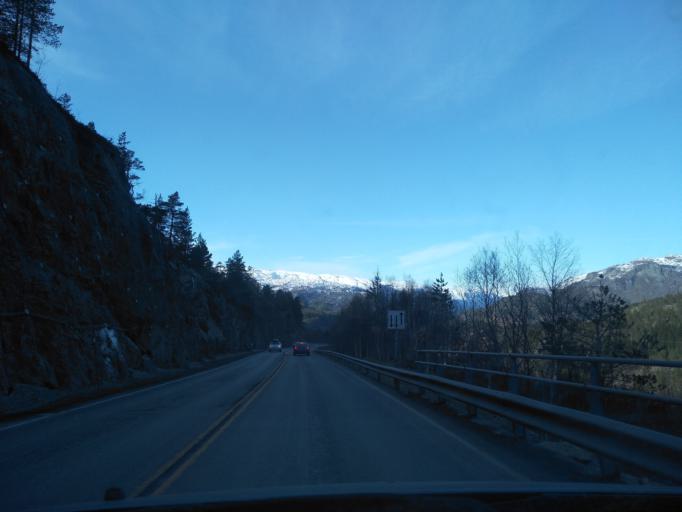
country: NO
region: Hordaland
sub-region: Odda
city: Odda
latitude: 59.9193
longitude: 6.6023
